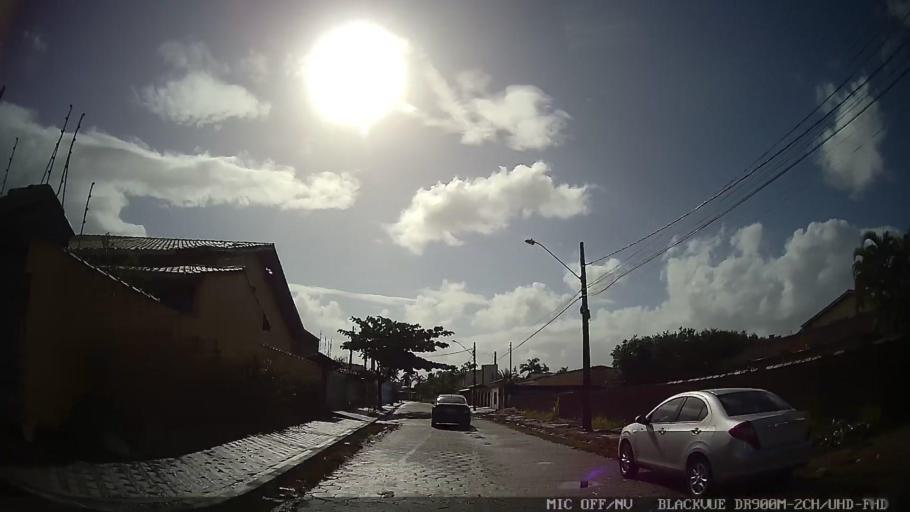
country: BR
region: Sao Paulo
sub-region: Itanhaem
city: Itanhaem
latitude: -24.2068
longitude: -46.8318
